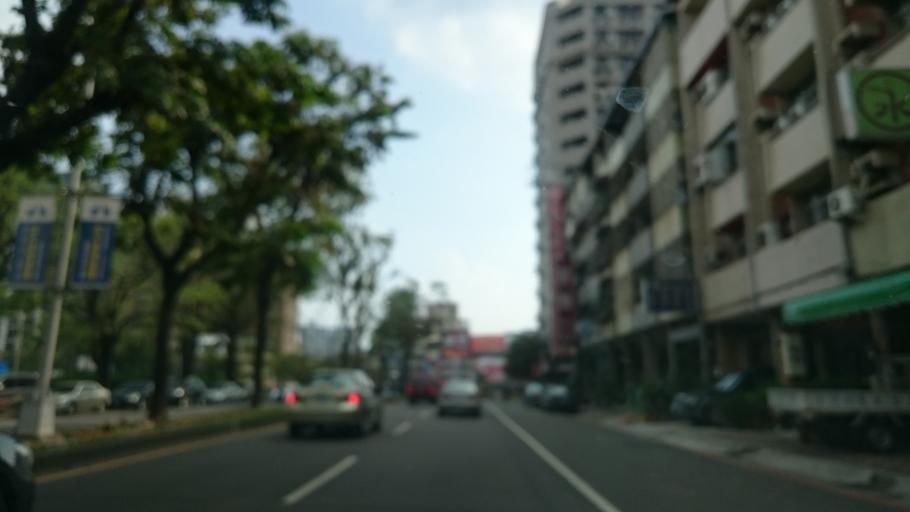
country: TW
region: Taiwan
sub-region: Taichung City
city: Taichung
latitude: 24.1314
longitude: 120.6573
